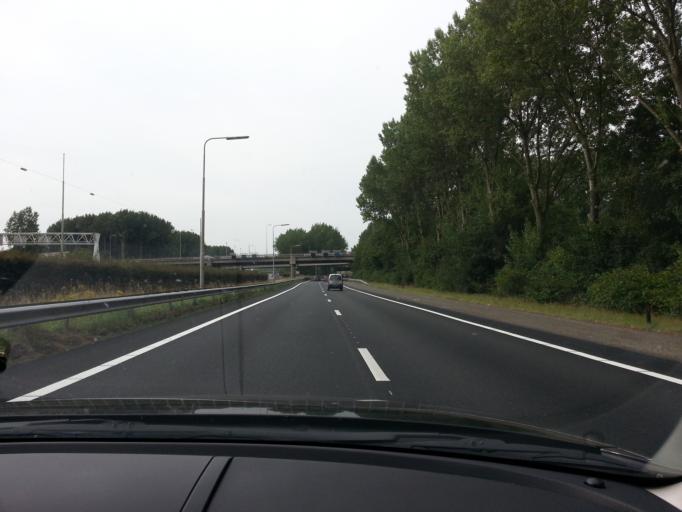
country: NL
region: South Holland
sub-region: Gemeente Ridderkerk
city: Ridderkerk
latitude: 51.8546
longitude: 4.6004
